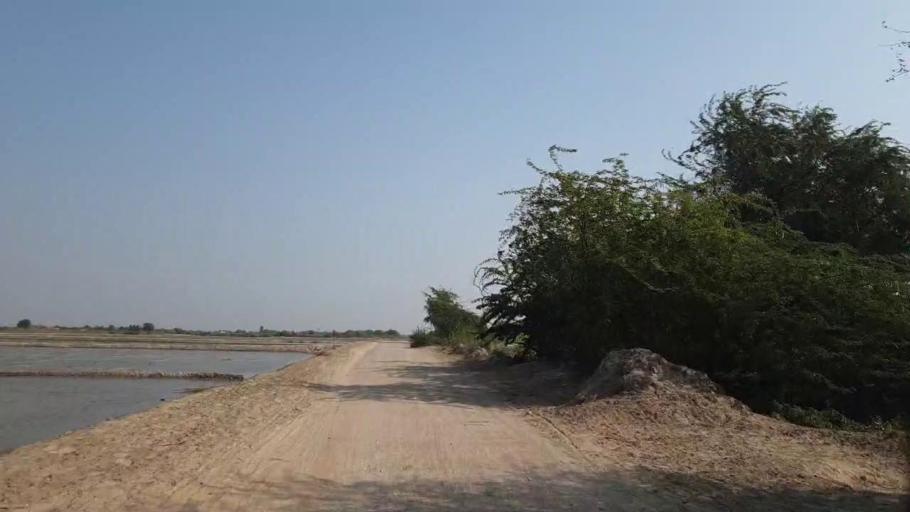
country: PK
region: Sindh
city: Bulri
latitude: 24.9345
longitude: 68.3660
